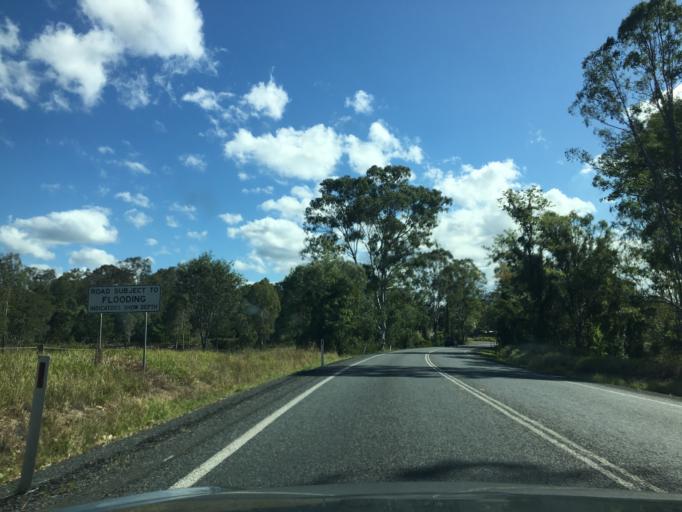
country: AU
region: Queensland
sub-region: Logan
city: Chambers Flat
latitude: -27.7557
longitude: 153.1180
